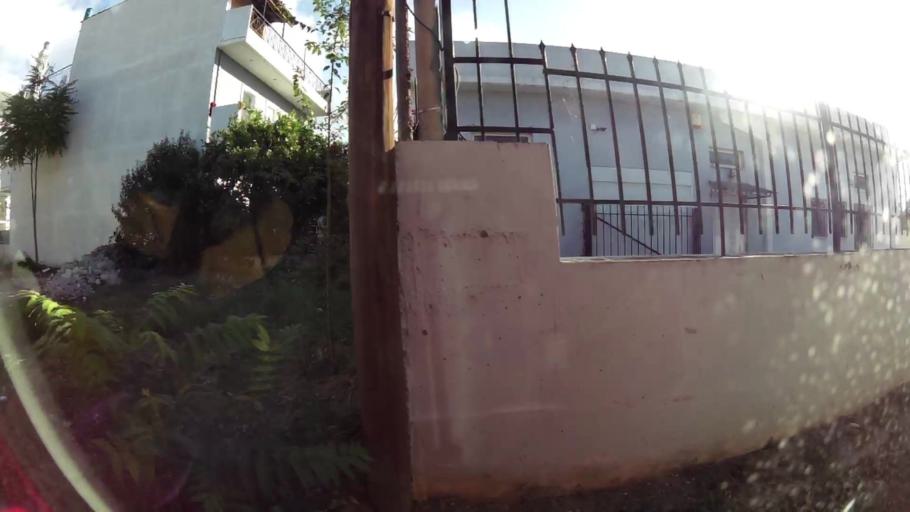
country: GR
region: Attica
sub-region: Nomarchia Anatolikis Attikis
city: Acharnes
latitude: 38.0719
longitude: 23.7460
